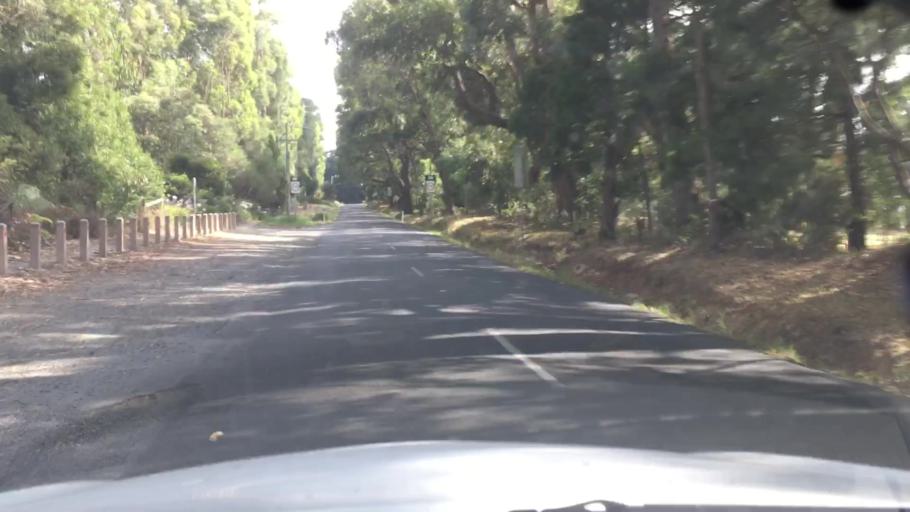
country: AU
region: Victoria
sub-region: Yarra Ranges
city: Macclesfield
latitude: -37.8887
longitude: 145.4759
